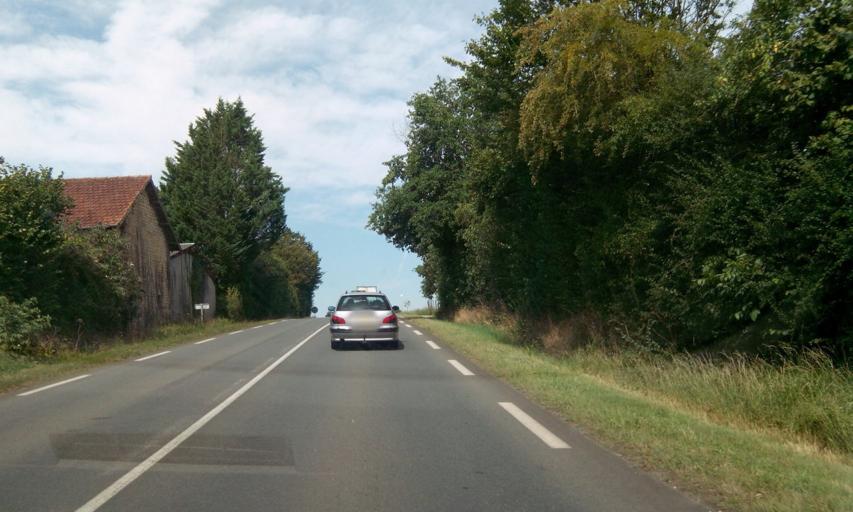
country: FR
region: Poitou-Charentes
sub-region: Departement des Deux-Sevres
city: Sauze-Vaussais
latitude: 46.1662
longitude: 0.0174
